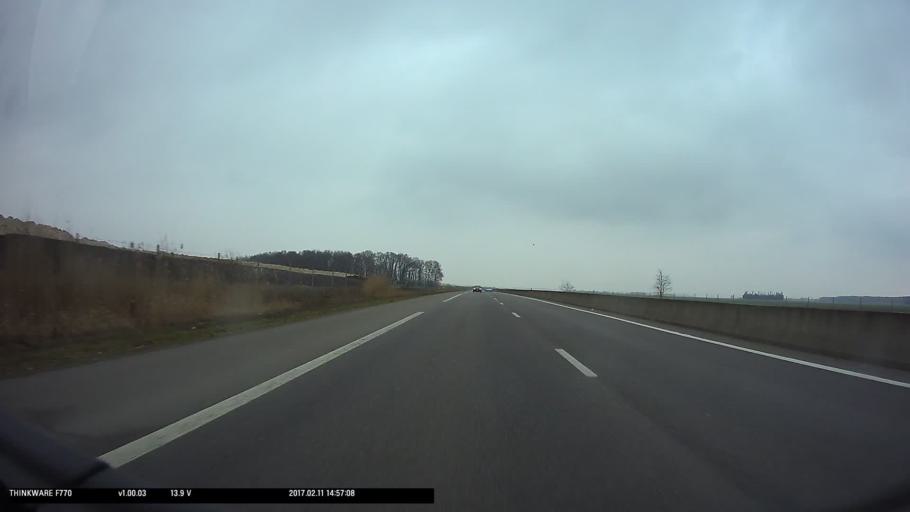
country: FR
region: Ile-de-France
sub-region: Departement des Yvelines
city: Rambouillet
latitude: 48.6070
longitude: 1.8317
